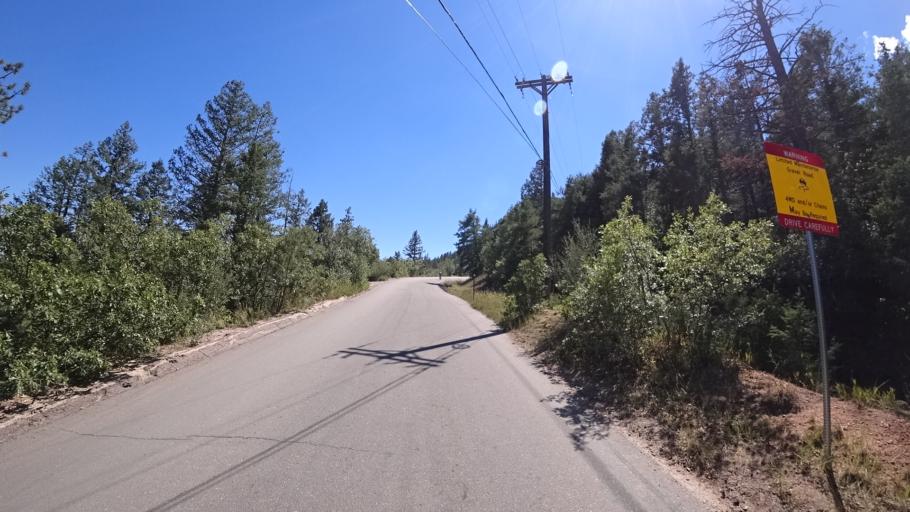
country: US
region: Colorado
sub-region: El Paso County
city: Colorado Springs
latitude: 38.7797
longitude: -104.8637
